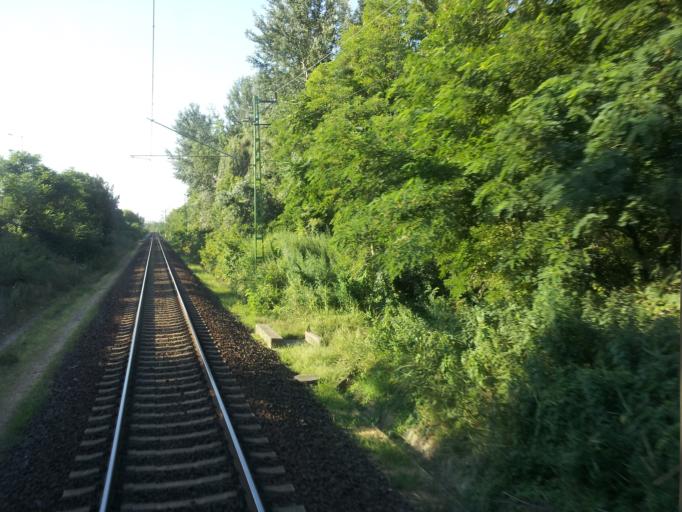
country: HU
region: Budapest
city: Budapest XX. keruelet
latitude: 47.4244
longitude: 19.1039
